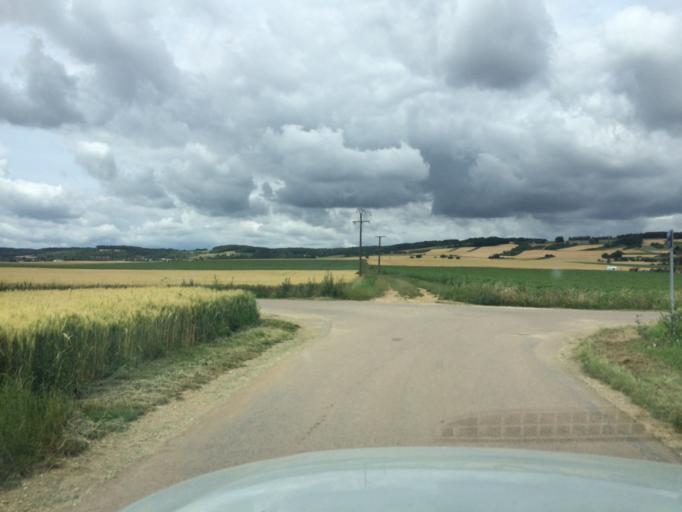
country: FR
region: Bourgogne
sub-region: Departement de l'Yonne
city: Aillant-sur-Tholon
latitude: 47.9248
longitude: 3.3563
